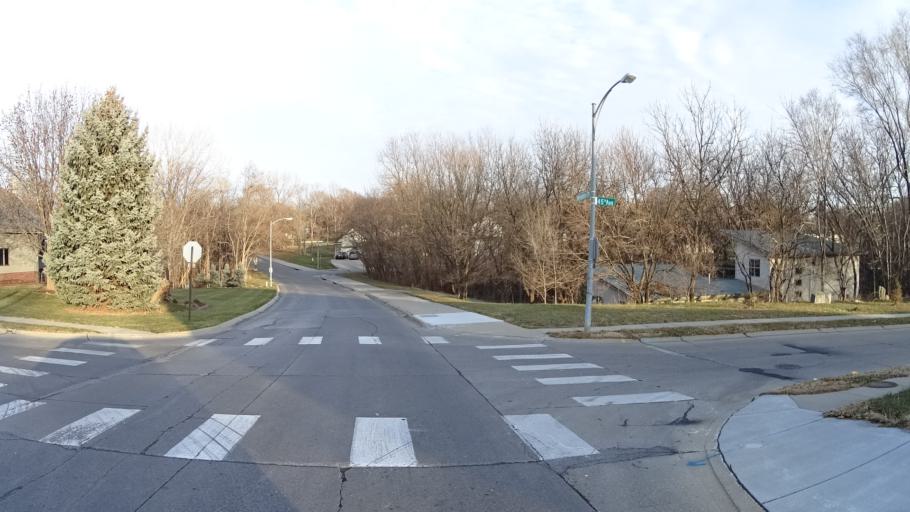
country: US
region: Nebraska
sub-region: Sarpy County
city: La Vista
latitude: 41.1832
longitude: -95.9835
